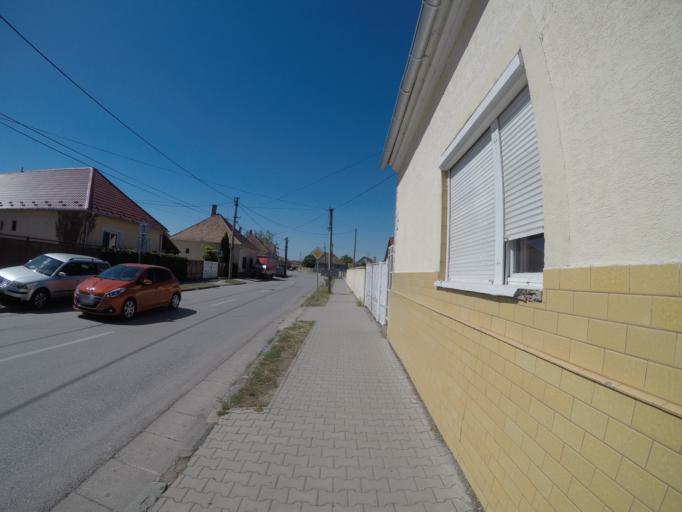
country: SK
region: Trnavsky
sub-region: Okres Dunajska Streda
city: Velky Meder
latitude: 47.8536
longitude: 17.7689
